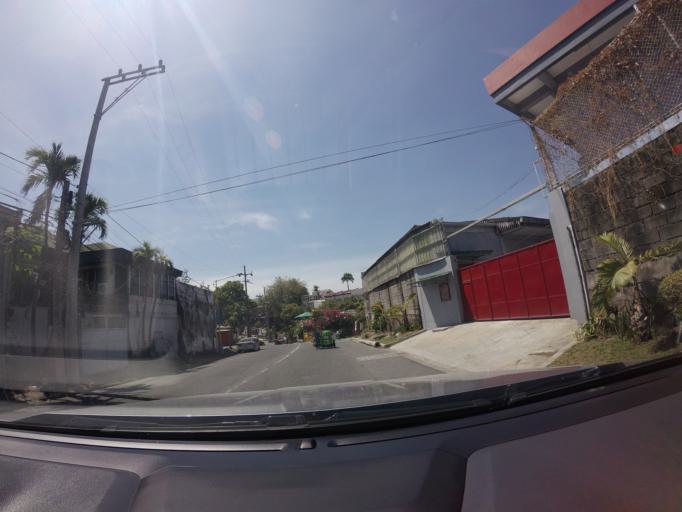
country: PH
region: Metro Manila
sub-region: Pasig
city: Pasig City
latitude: 14.5684
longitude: 121.0559
